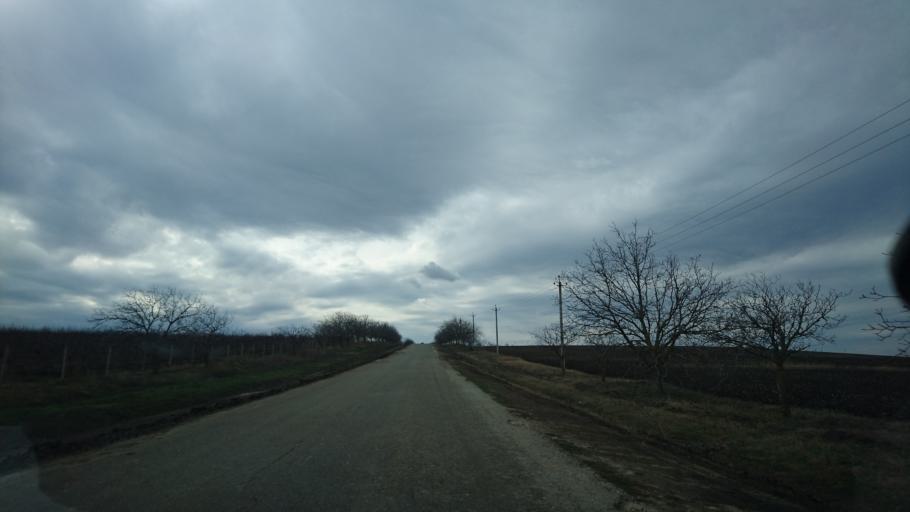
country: MD
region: Cantemir
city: Visniovca
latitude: 46.3247
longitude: 28.4834
